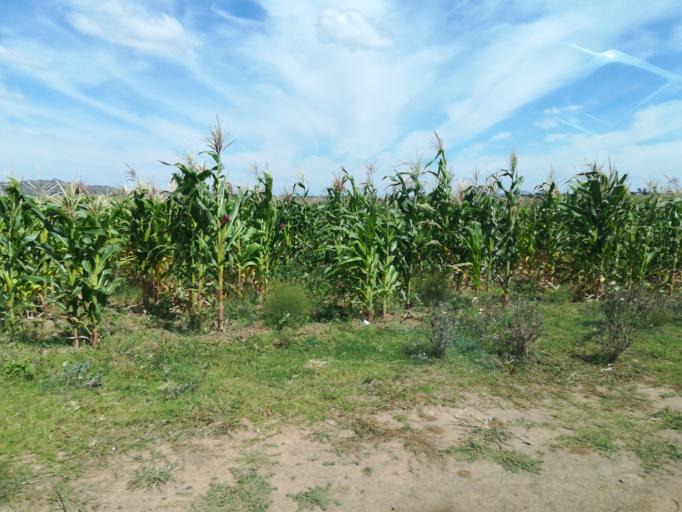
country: LS
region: Mohale's Hoek District
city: Mohale's Hoek
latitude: -30.1064
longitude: 27.4663
